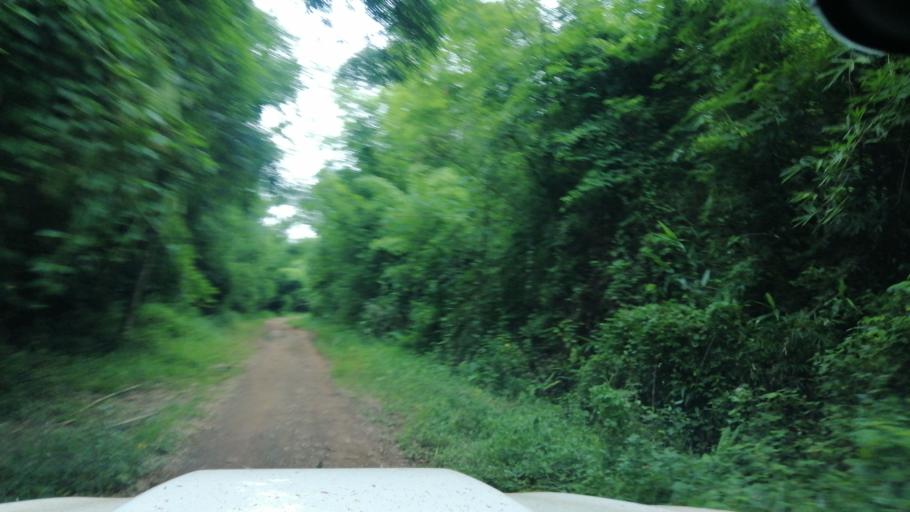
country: TH
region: Nan
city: Mae Charim
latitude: 18.7451
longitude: 101.2849
